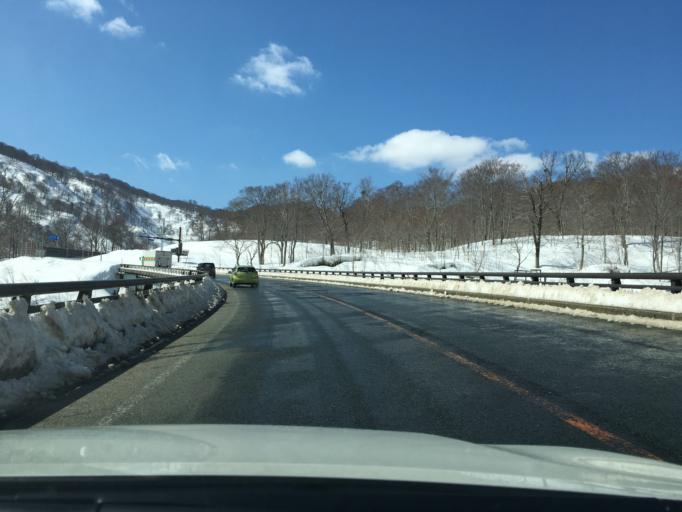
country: JP
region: Yamagata
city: Tsuruoka
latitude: 38.4941
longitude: 139.9762
